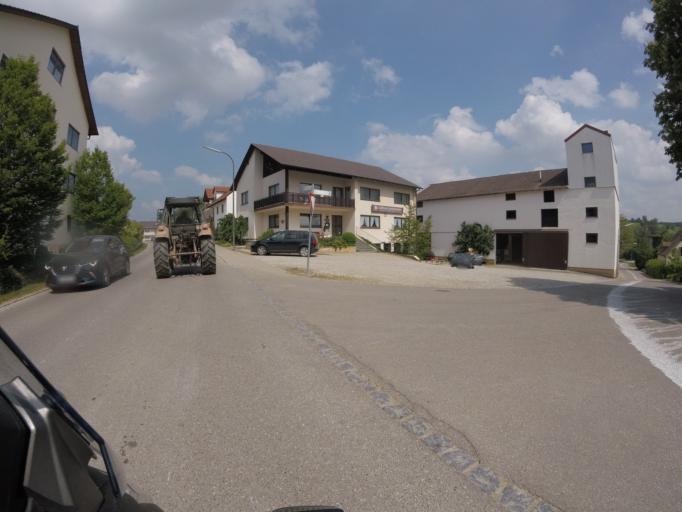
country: DE
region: Bavaria
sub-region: Upper Bavaria
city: Wolnzach
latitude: 48.5611
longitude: 11.6278
